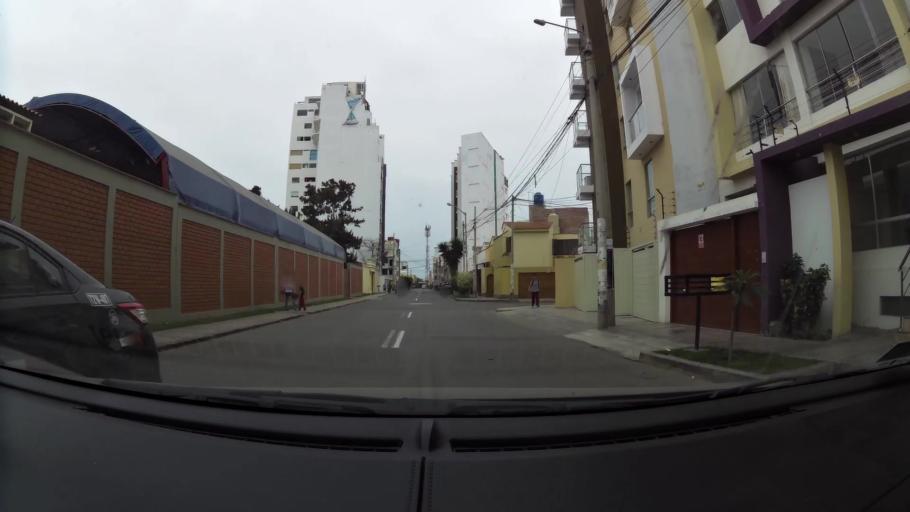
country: PE
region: La Libertad
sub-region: Provincia de Trujillo
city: Buenos Aires
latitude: -8.1339
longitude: -79.0407
